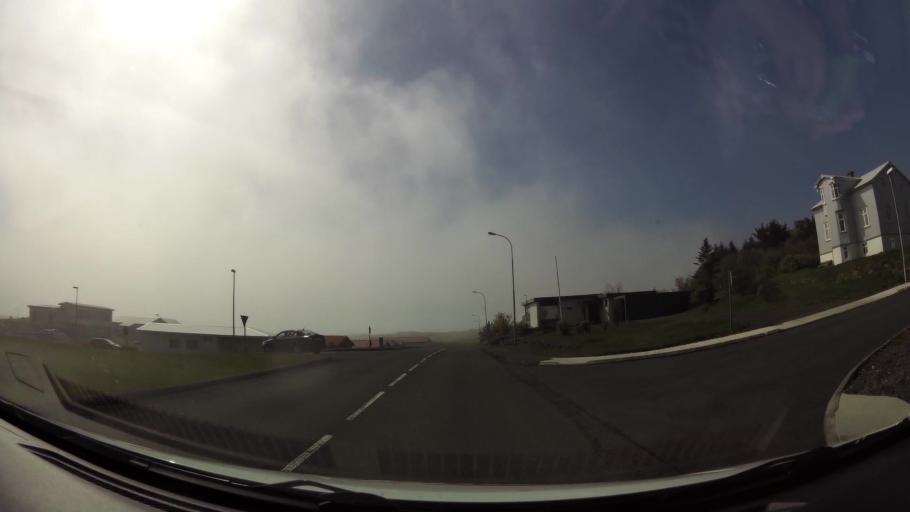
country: IS
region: East
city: Reydarfjoerdur
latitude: 64.6558
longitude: -14.2877
